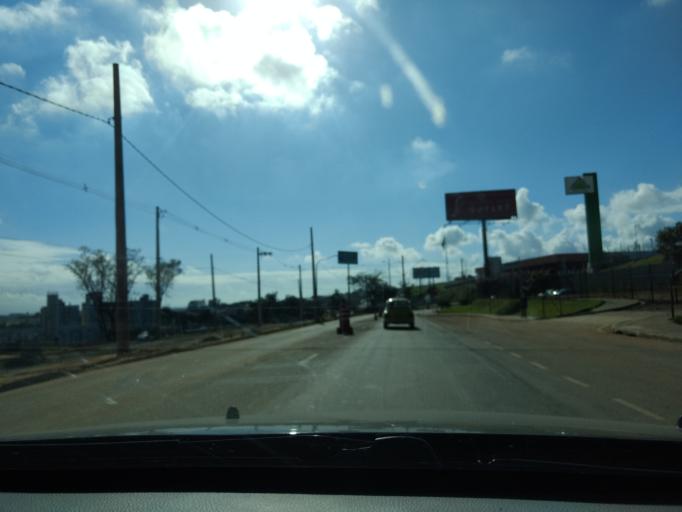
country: BR
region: Sao Paulo
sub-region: Taubate
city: Taubate
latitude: -23.0157
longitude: -45.5262
